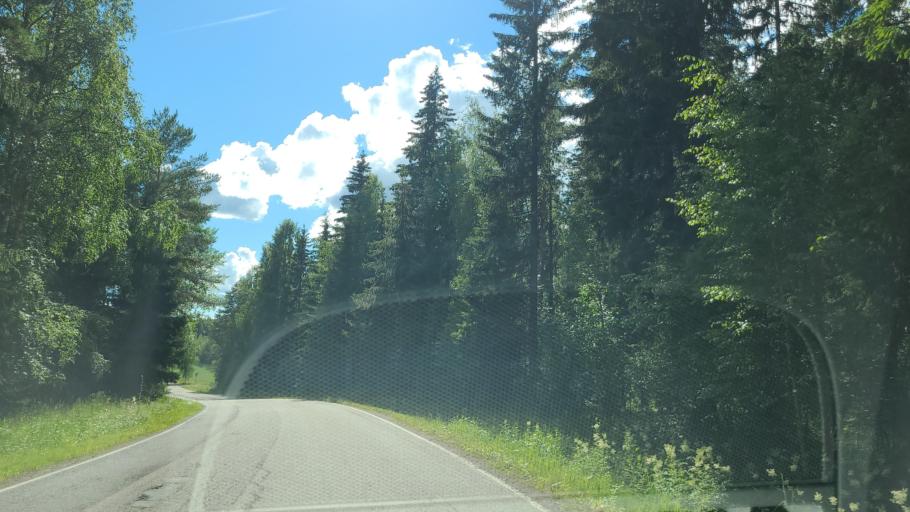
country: FI
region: Central Finland
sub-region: Jaemsae
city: Jaemsae
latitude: 61.8852
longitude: 25.2383
